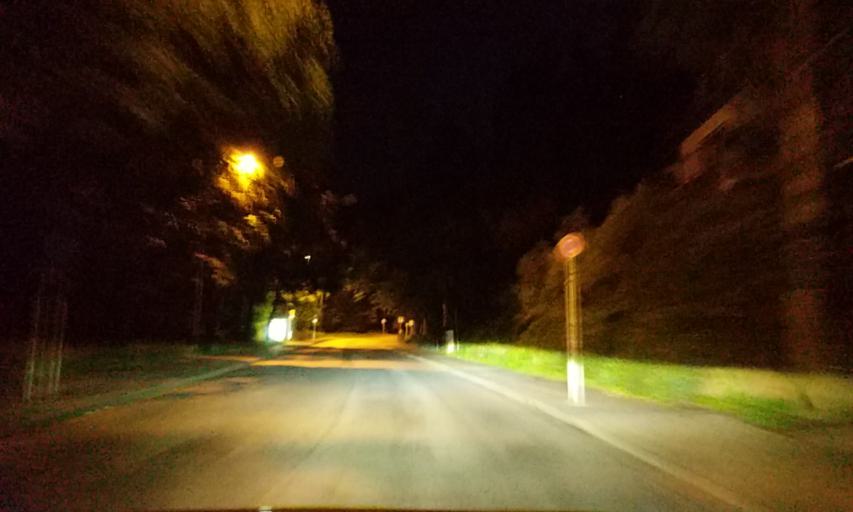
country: DE
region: Rheinland-Pfalz
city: Kaiserslautern
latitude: 49.4354
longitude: 7.7823
